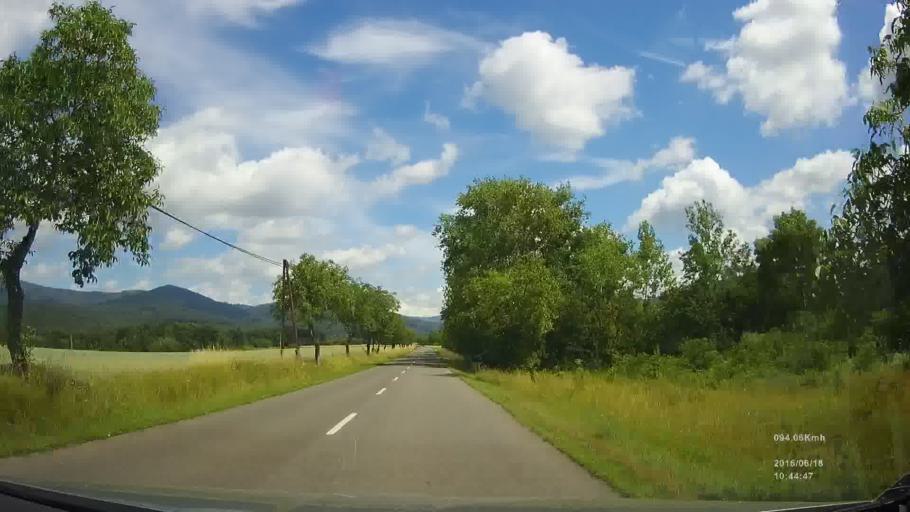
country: SK
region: Kosicky
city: Sobrance
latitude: 48.8288
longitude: 22.1747
